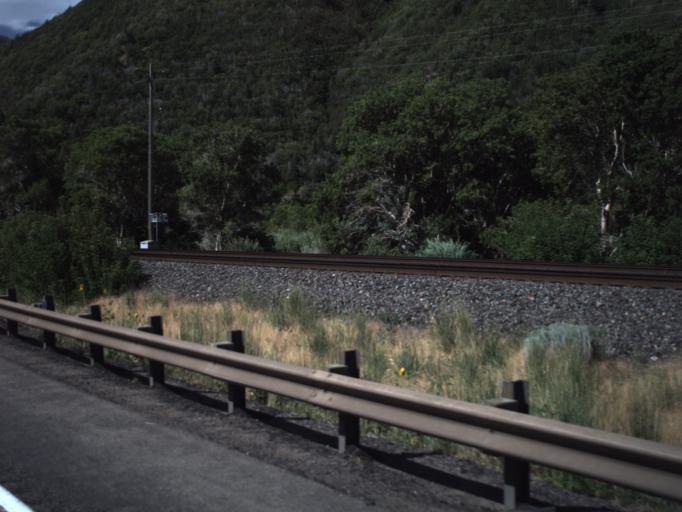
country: US
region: Utah
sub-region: Utah County
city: Mapleton
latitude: 40.0491
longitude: -111.5478
